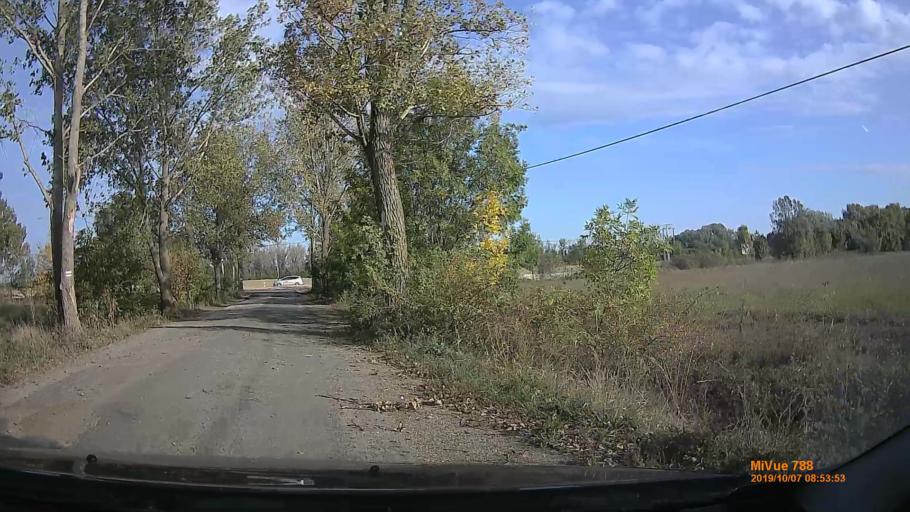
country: HU
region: Bekes
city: Szarvas
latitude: 46.8197
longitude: 20.5250
